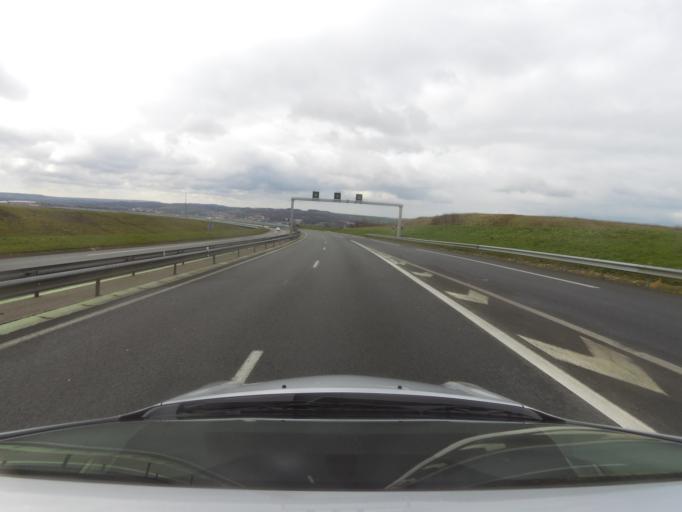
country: FR
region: Nord-Pas-de-Calais
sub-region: Departement du Pas-de-Calais
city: Saint-Leonard
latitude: 50.7061
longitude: 1.6348
